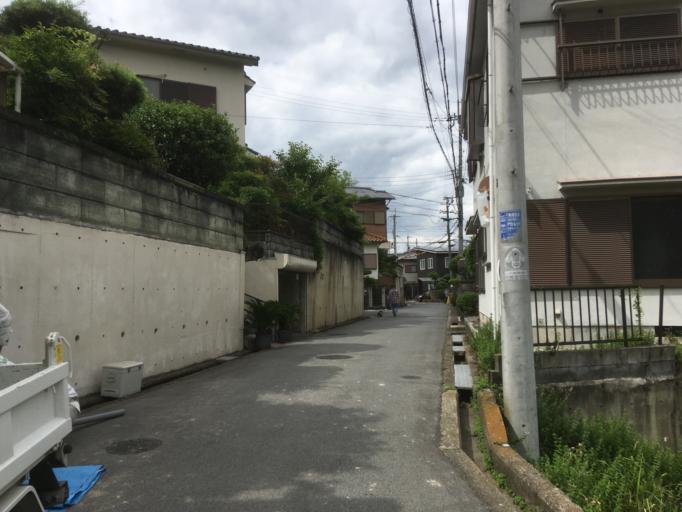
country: JP
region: Nara
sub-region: Ikoma-shi
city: Ikoma
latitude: 34.6739
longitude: 135.7017
